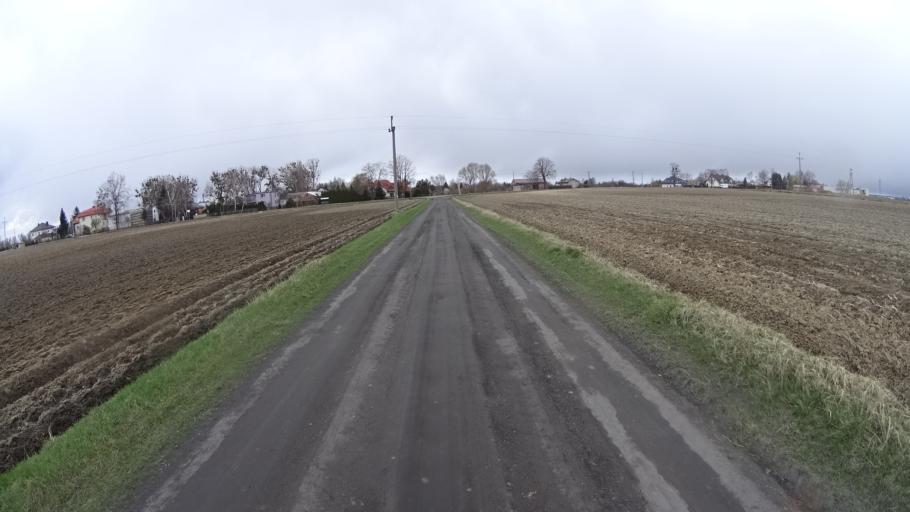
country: PL
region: Masovian Voivodeship
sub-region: Powiat warszawski zachodni
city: Blonie
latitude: 52.2164
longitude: 20.6552
